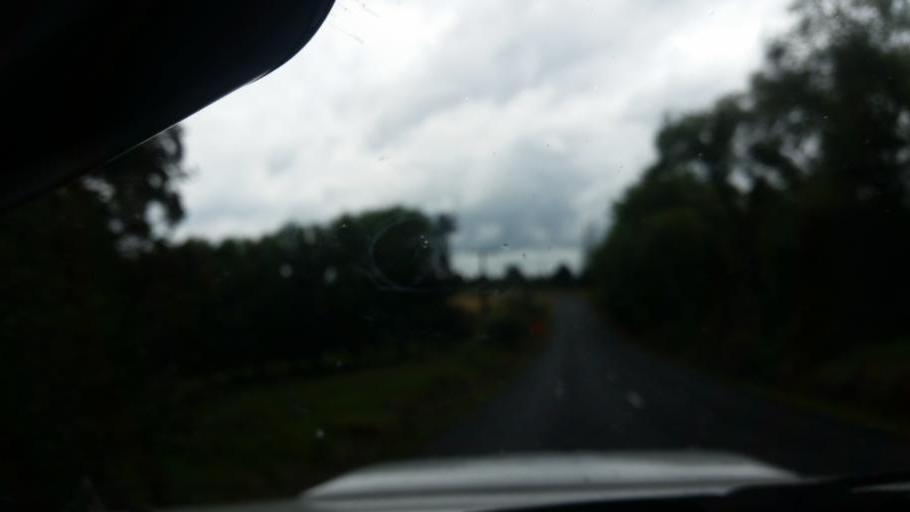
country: NZ
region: Auckland
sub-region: Auckland
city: Wellsford
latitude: -36.1478
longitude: 174.2223
